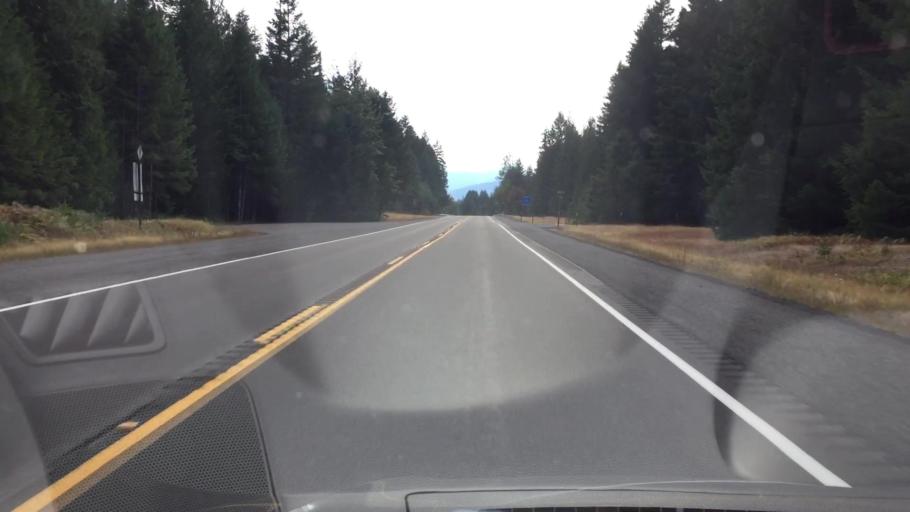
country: US
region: Washington
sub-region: Pierce County
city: Buckley
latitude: 46.6501
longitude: -121.6101
